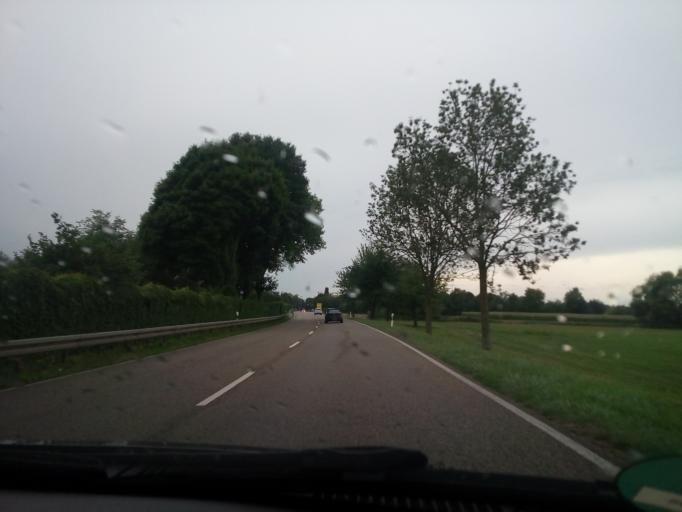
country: DE
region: Baden-Wuerttemberg
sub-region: Karlsruhe Region
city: Buhl
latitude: 48.7006
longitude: 8.1216
